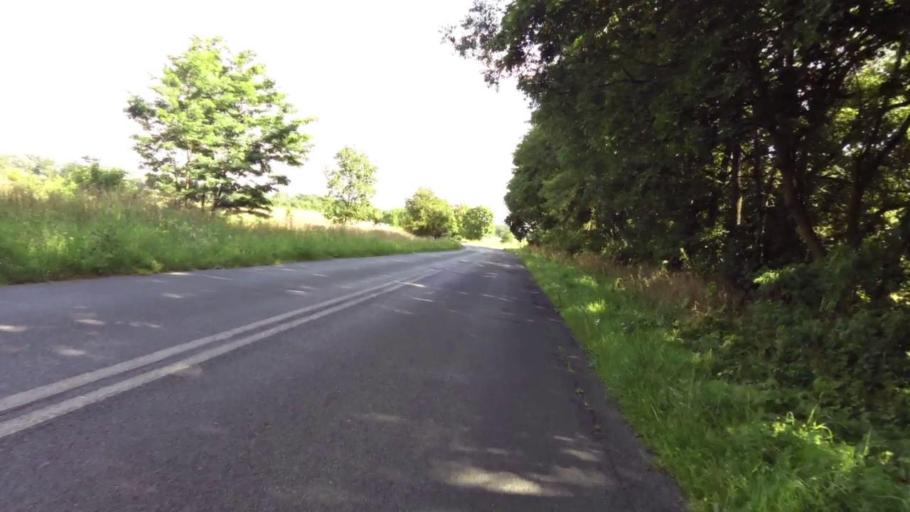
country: PL
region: West Pomeranian Voivodeship
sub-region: Powiat stargardzki
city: Dobrzany
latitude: 53.3732
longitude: 15.4341
